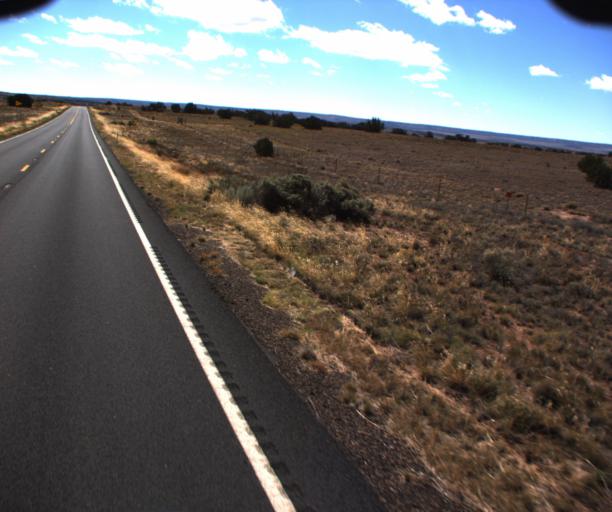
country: US
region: Arizona
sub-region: Apache County
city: Houck
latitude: 35.1143
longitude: -109.3207
